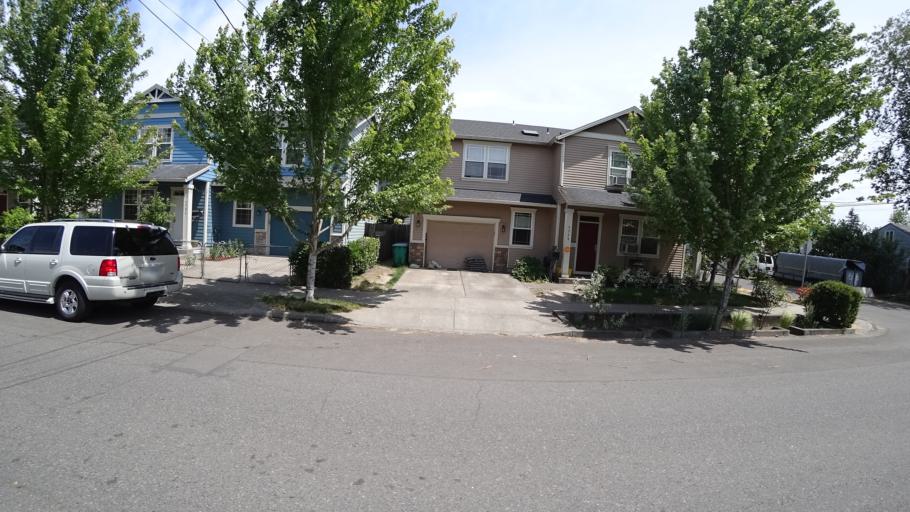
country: US
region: Oregon
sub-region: Multnomah County
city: Lents
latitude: 45.4675
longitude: -122.6022
